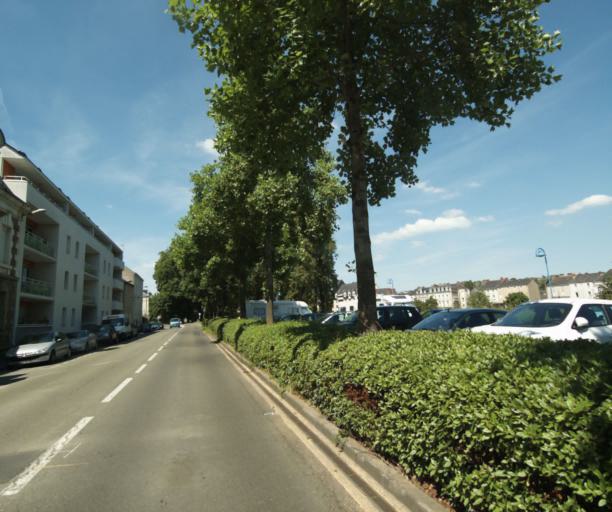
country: FR
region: Pays de la Loire
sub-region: Departement de la Mayenne
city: Laval
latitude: 48.0776
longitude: -0.7712
